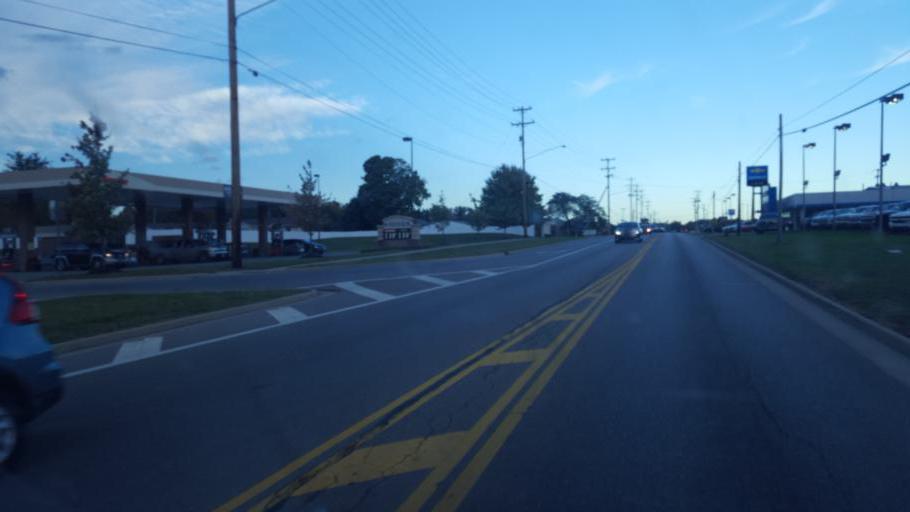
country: US
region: Ohio
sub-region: Licking County
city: Johnstown
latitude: 40.1454
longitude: -82.7057
